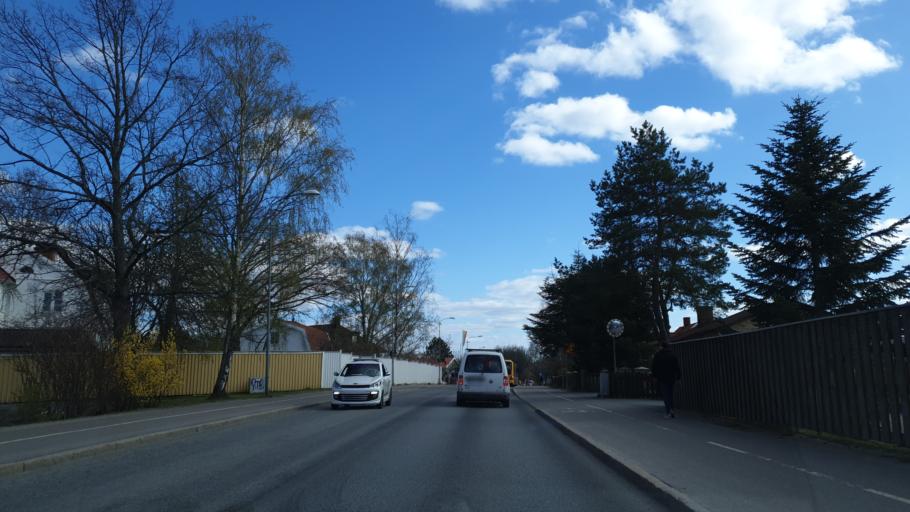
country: SE
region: Uppsala
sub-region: Uppsala Kommun
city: Gamla Uppsala
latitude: 59.8939
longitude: 17.6376
